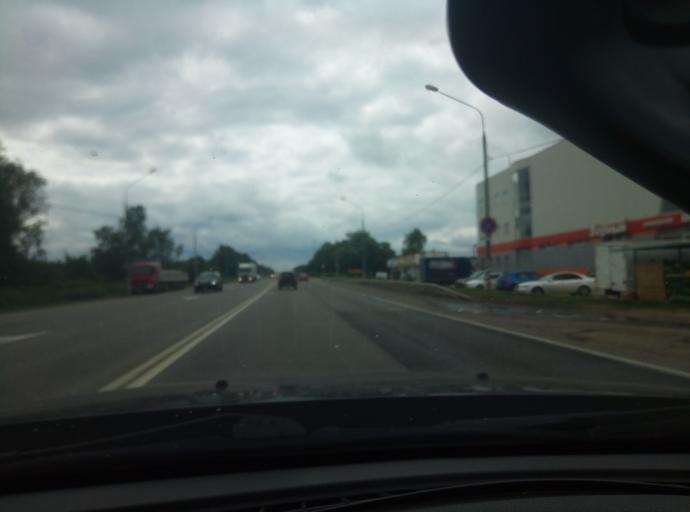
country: RU
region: Kaluga
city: Obninsk
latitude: 55.0927
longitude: 36.6355
